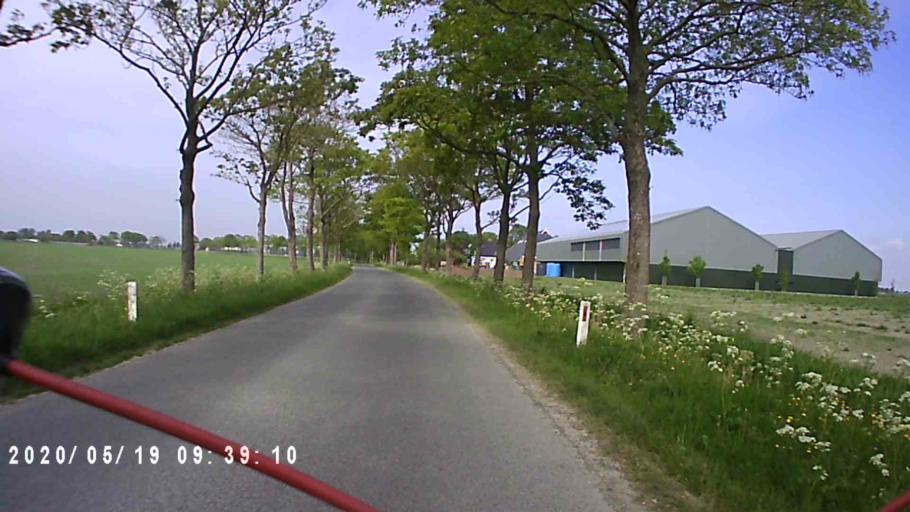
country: NL
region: Groningen
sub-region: Gemeente Zuidhorn
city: Grijpskerk
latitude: 53.2891
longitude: 6.2815
